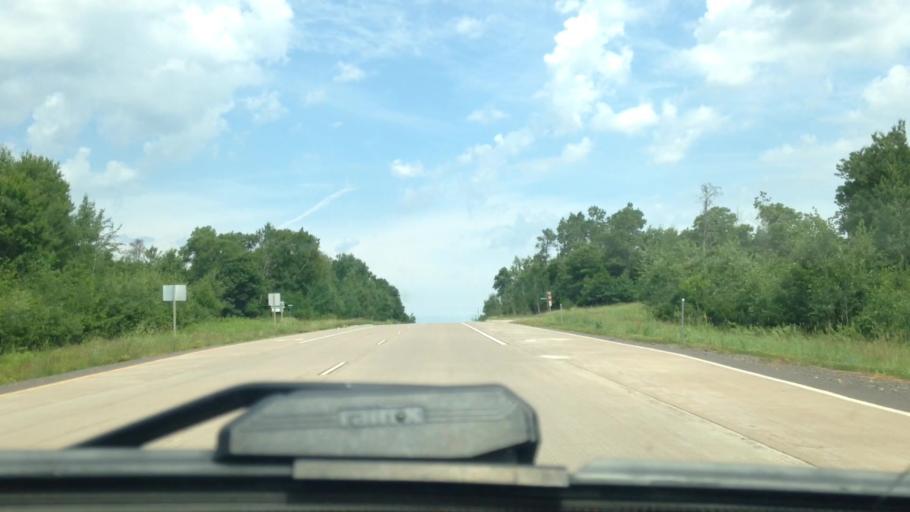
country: US
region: Wisconsin
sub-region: Douglas County
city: Lake Nebagamon
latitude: 46.2727
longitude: -91.8049
